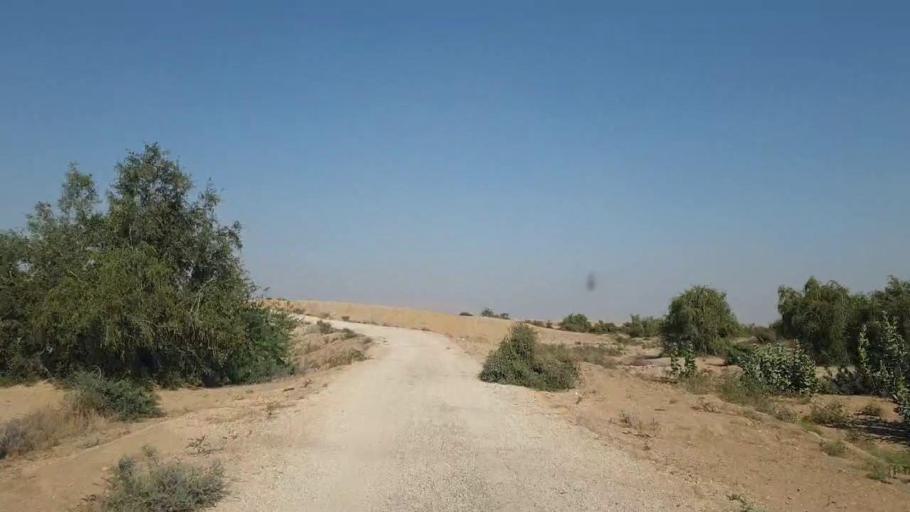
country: PK
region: Sindh
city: Jamshoro
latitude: 25.4844
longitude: 67.8394
